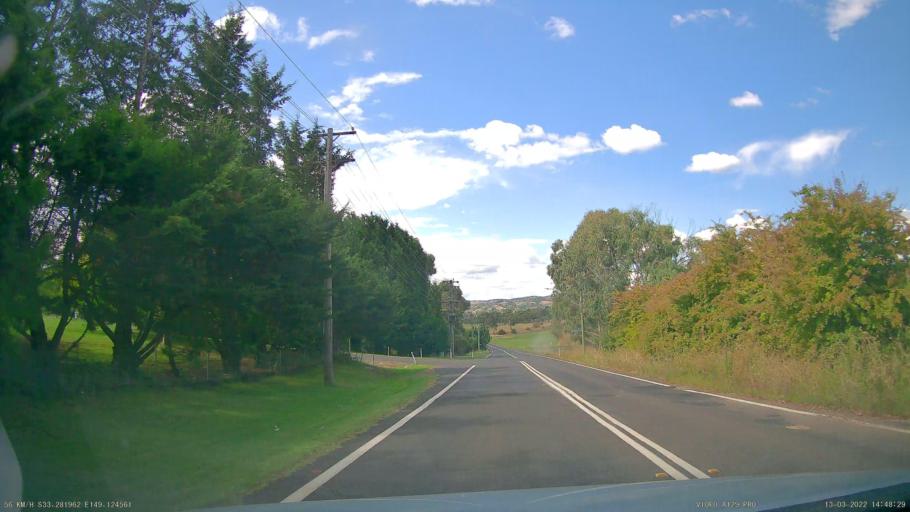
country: AU
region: New South Wales
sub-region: Orange Municipality
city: Orange
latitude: -33.2817
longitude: 149.1249
